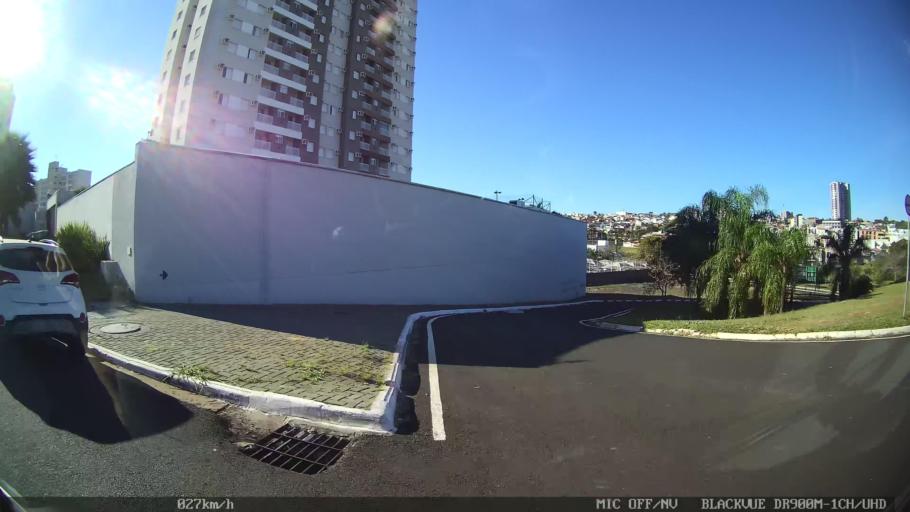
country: BR
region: Sao Paulo
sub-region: Franca
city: Franca
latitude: -20.5518
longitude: -47.4065
